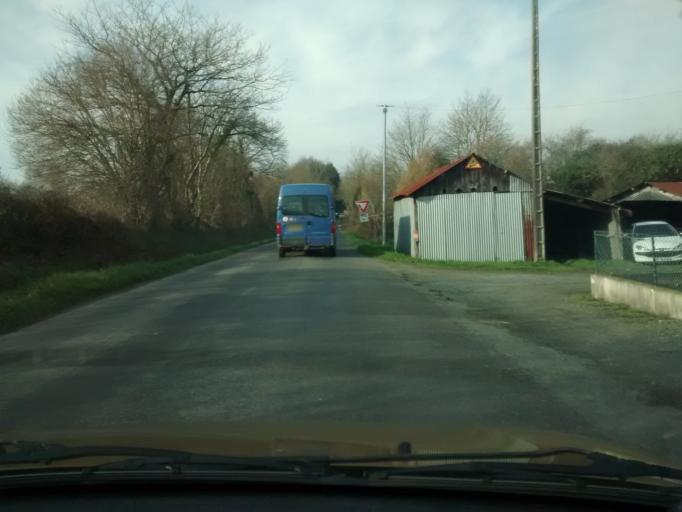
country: FR
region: Pays de la Loire
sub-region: Departement de la Loire-Atlantique
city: Notre-Dame-des-Landes
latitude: 47.3687
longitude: -1.7276
